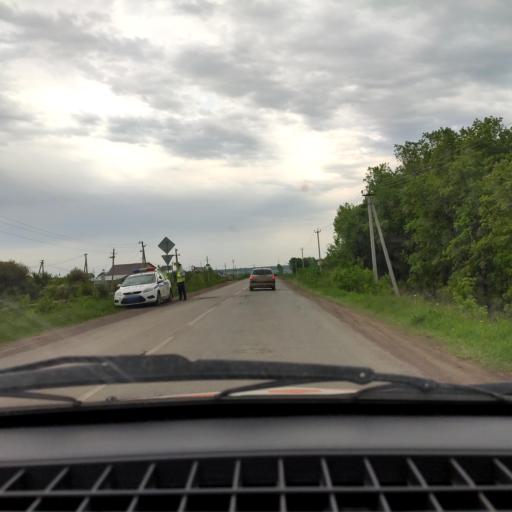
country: RU
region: Bashkortostan
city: Avdon
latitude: 54.5791
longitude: 55.7515
